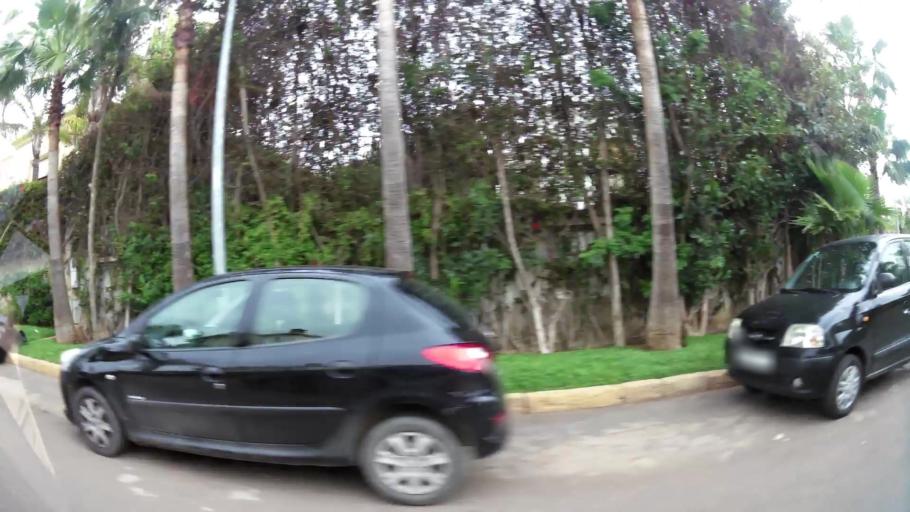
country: MA
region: Grand Casablanca
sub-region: Casablanca
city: Casablanca
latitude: 33.5250
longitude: -7.6334
